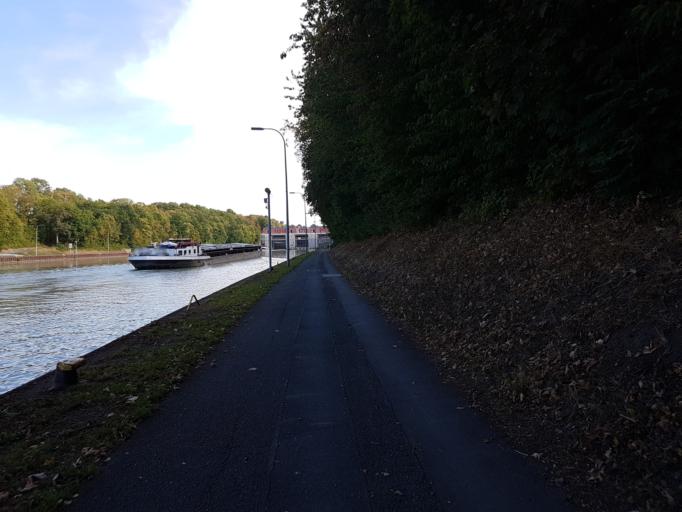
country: DE
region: Lower Saxony
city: Laatzen
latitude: 52.3651
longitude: 9.8596
